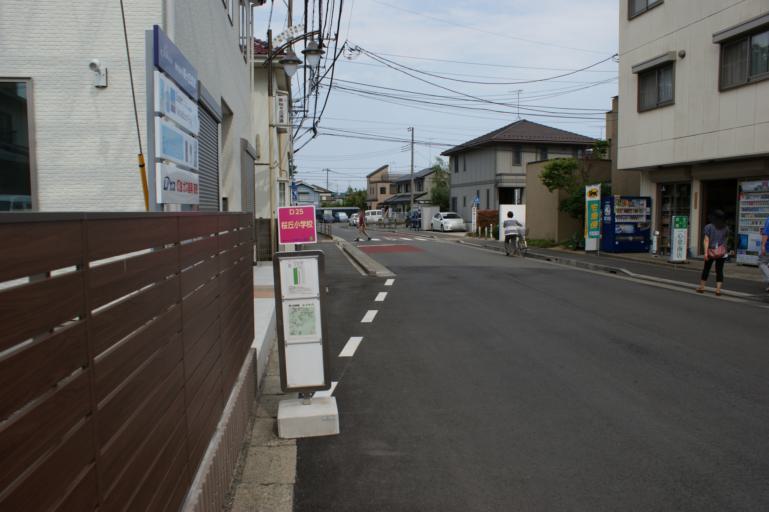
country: JP
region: Kanagawa
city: Minami-rinkan
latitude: 35.4525
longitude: 139.4675
